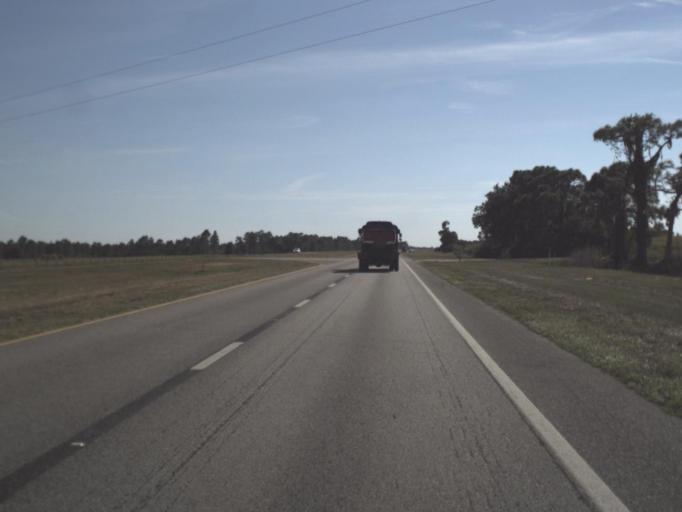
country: US
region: Florida
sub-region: Highlands County
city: Placid Lakes
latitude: 27.0819
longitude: -81.3349
